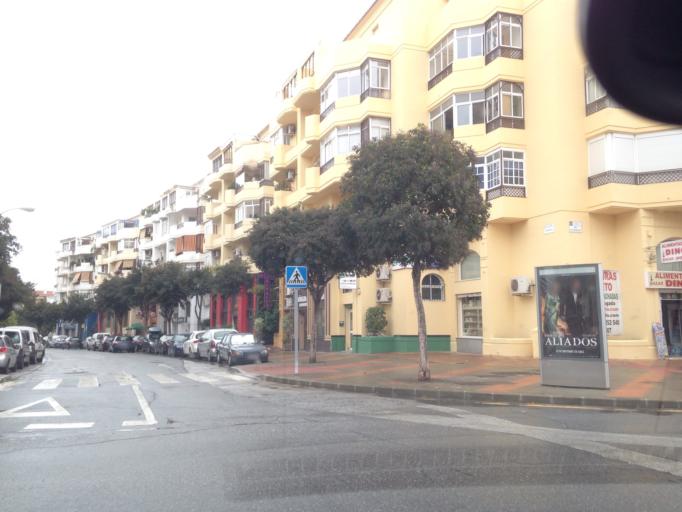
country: ES
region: Andalusia
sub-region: Provincia de Malaga
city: Malaga
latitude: 36.7176
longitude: -4.4558
